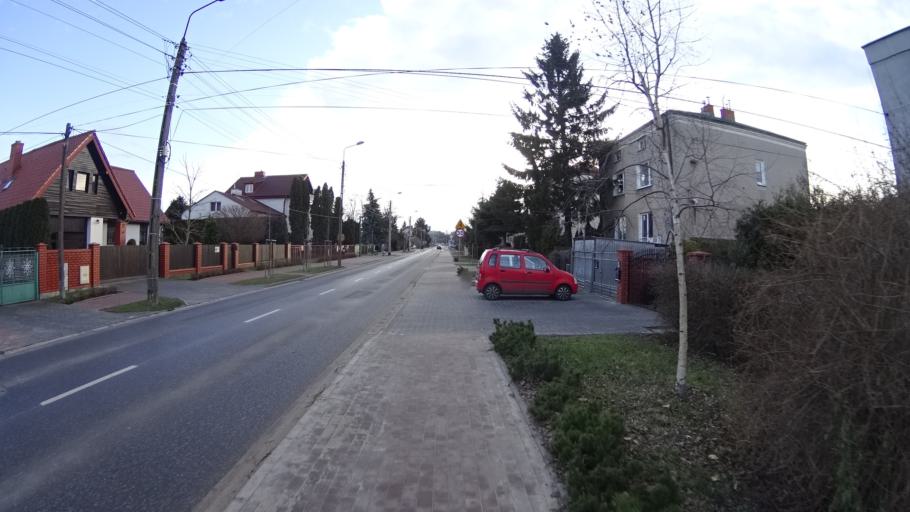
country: PL
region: Masovian Voivodeship
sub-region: Powiat warszawski zachodni
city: Ozarow Mazowiecki
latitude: 52.2174
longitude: 20.8000
